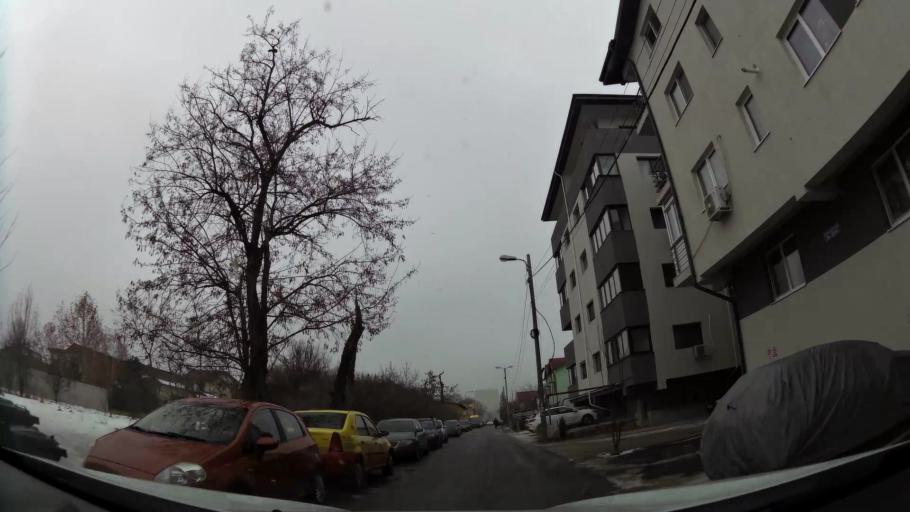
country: RO
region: Ilfov
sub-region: Comuna Popesti-Leordeni
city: Popesti-Leordeni
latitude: 44.4036
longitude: 26.1726
